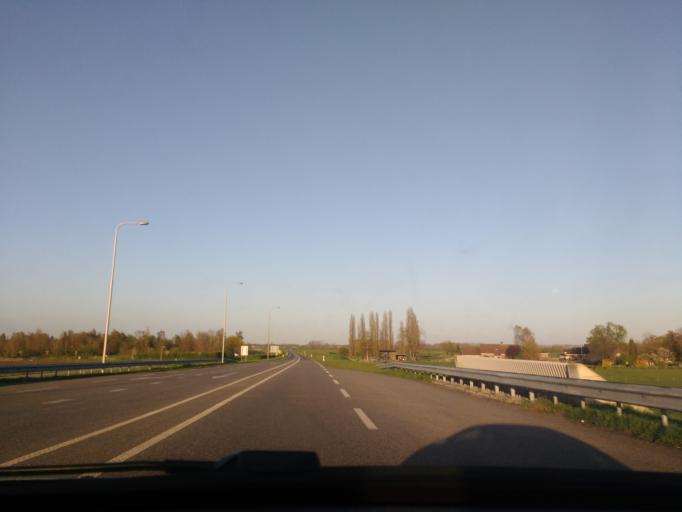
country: NL
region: Gelderland
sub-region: Gemeente Overbetuwe
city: Heteren
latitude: 51.9456
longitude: 5.7687
